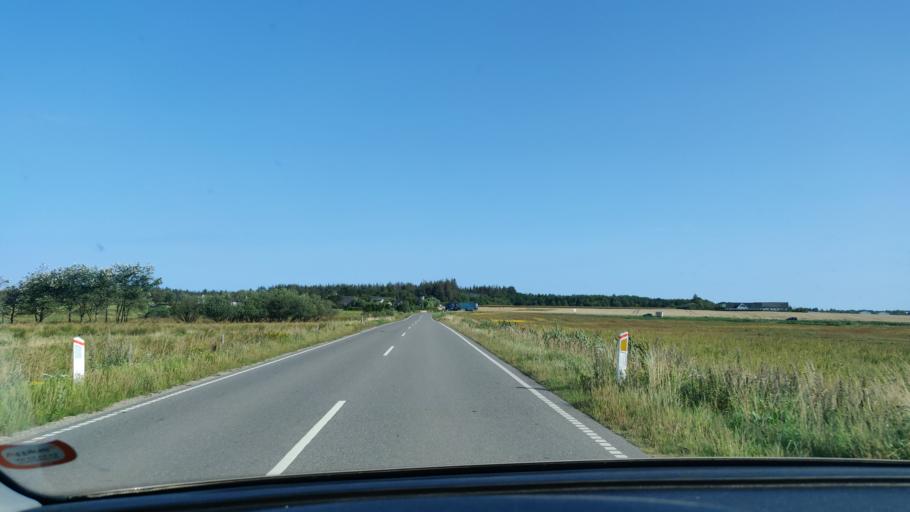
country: DK
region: North Denmark
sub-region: Jammerbugt Kommune
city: Pandrup
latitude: 57.2429
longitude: 9.6474
